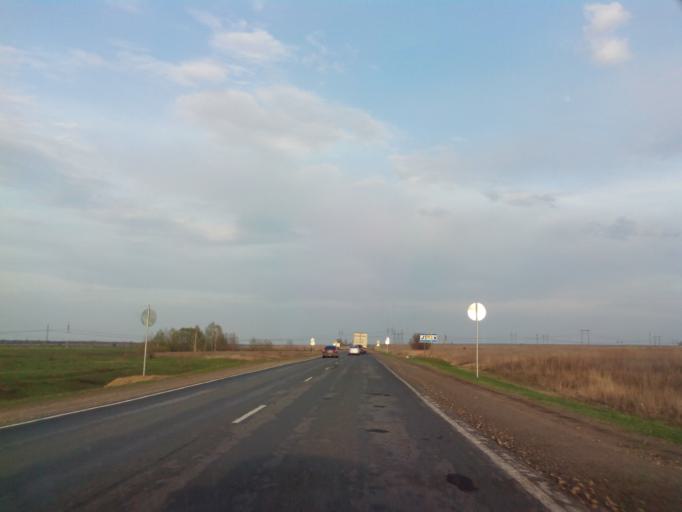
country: RU
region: Rjazan
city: Korablino
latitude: 53.7500
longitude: 39.8528
